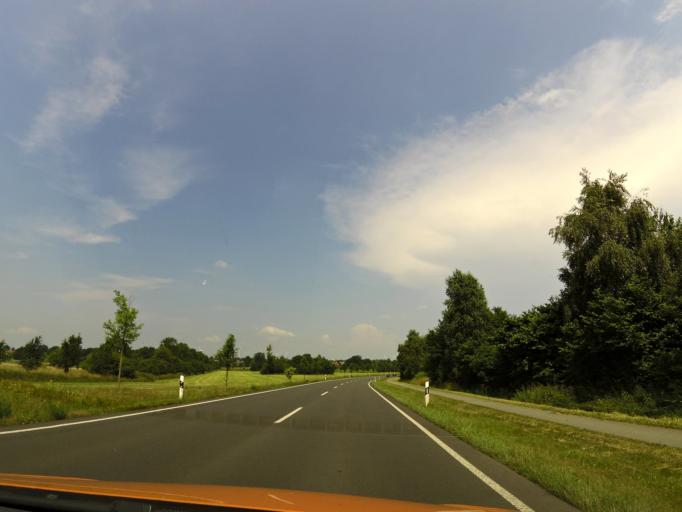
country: DE
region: Brandenburg
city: Gerdshagen
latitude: 53.2003
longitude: 12.2036
